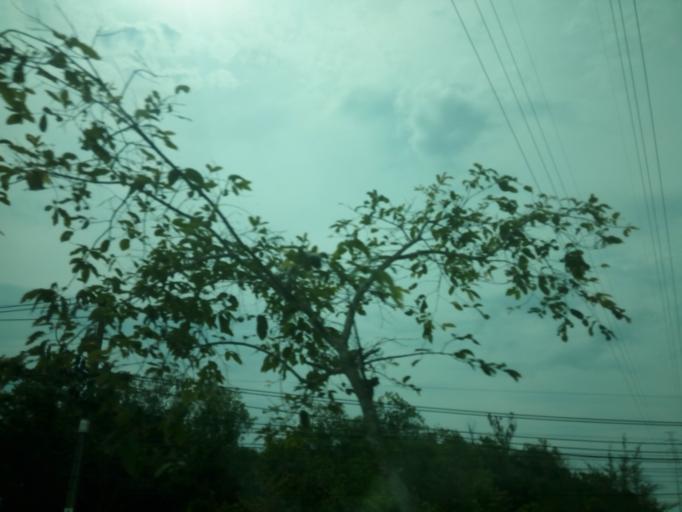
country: TH
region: Krabi
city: Khlong Thom
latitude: 8.0159
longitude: 99.1165
